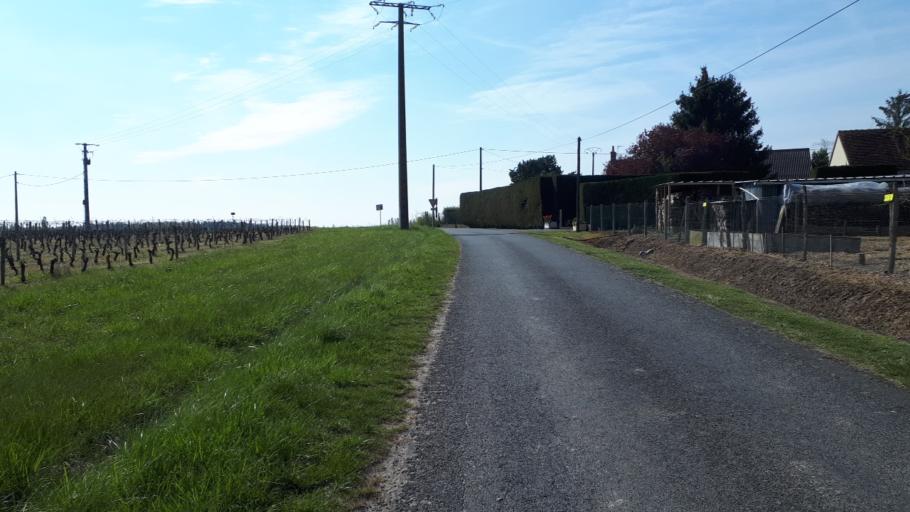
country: FR
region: Centre
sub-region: Departement du Loir-et-Cher
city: Saint-Romain-sur-Cher
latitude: 47.3667
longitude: 1.3902
